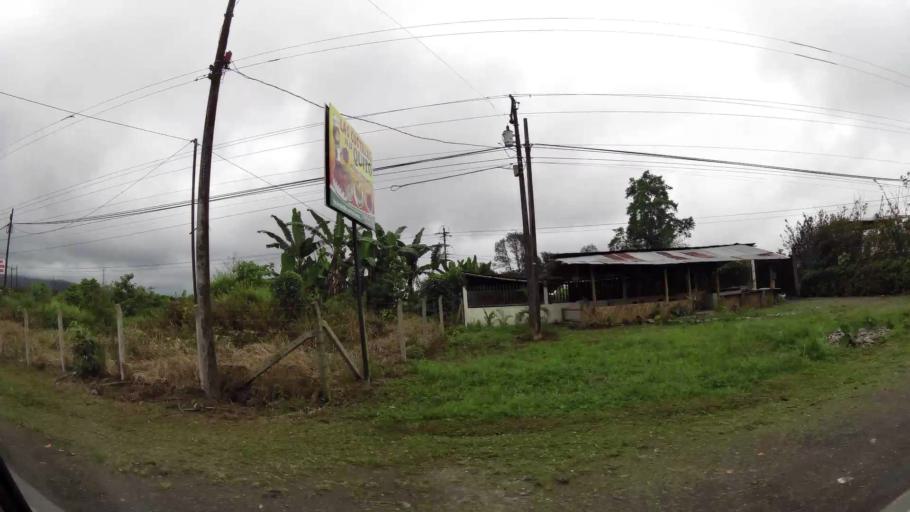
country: EC
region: Santo Domingo de los Tsachilas
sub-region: Canton Santo Domingo de los Colorados
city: Santo Domingo de los Colorados
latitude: -0.2561
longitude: -79.1274
